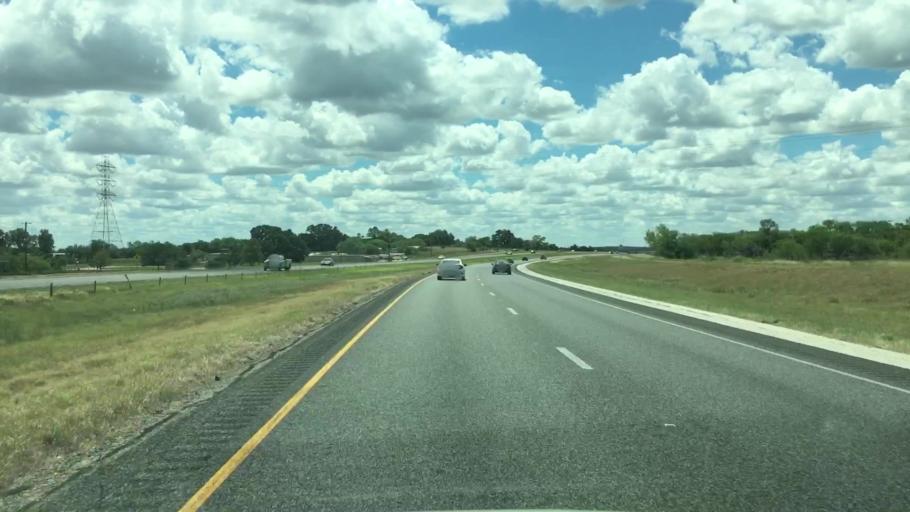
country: US
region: Texas
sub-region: Bexar County
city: Elmendorf
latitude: 29.2503
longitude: -98.3953
